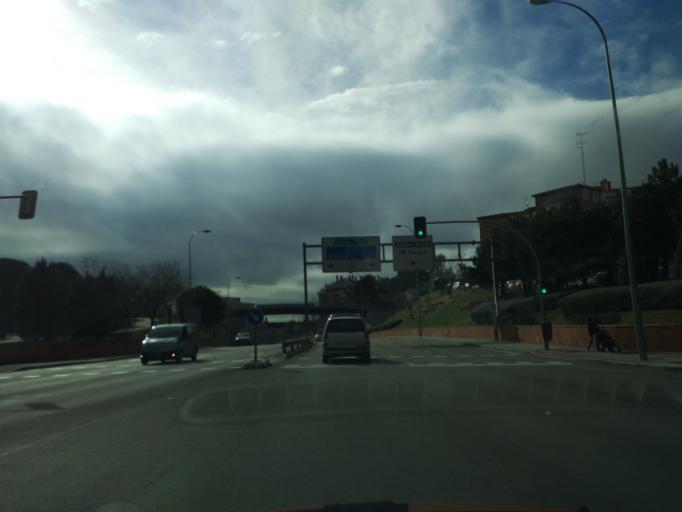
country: ES
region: Madrid
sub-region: Provincia de Madrid
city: Ciudad Lineal
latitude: 40.4669
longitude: -3.6544
